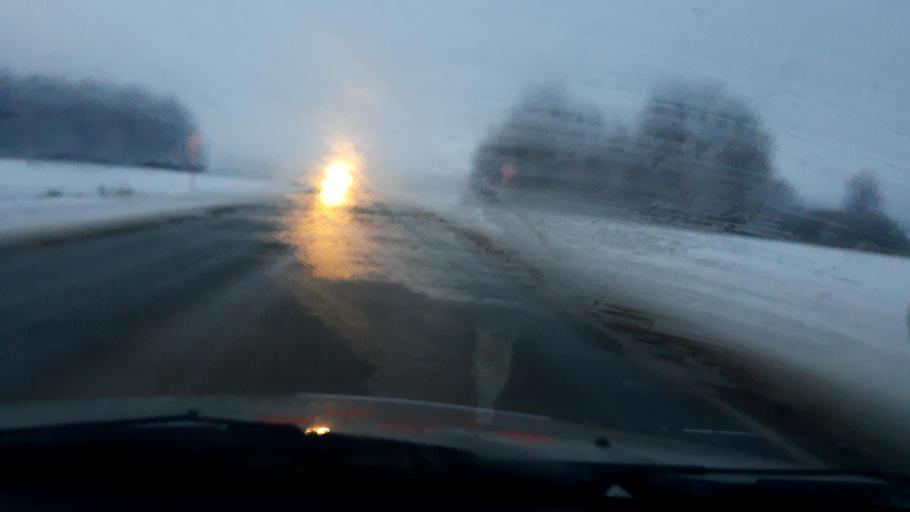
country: RU
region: Bashkortostan
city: Avdon
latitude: 54.6903
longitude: 55.7471
